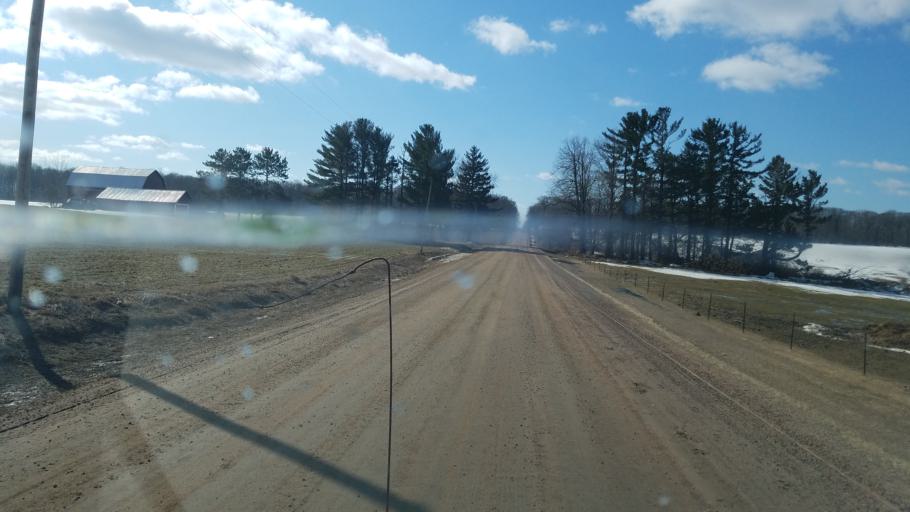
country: US
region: Wisconsin
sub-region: Clark County
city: Loyal
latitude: 44.6666
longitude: -90.4560
